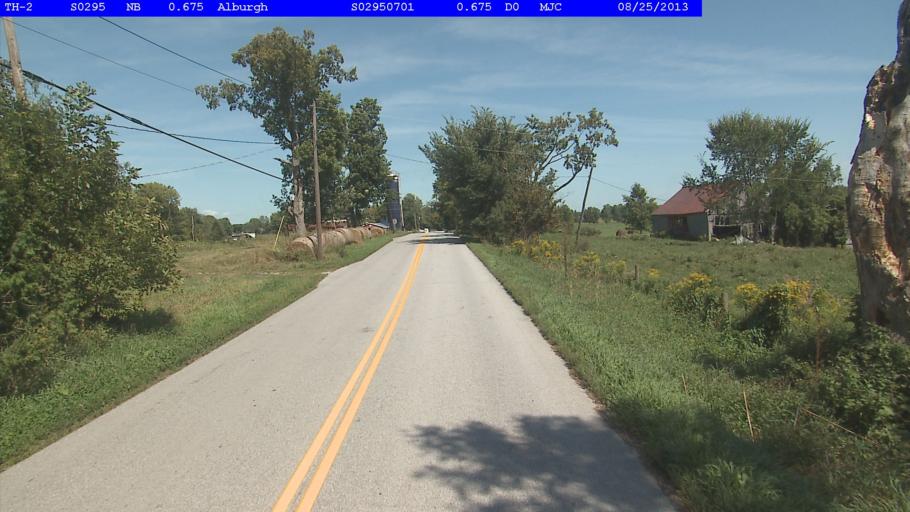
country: US
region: Vermont
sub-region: Franklin County
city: Swanton
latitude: 44.9838
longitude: -73.2272
